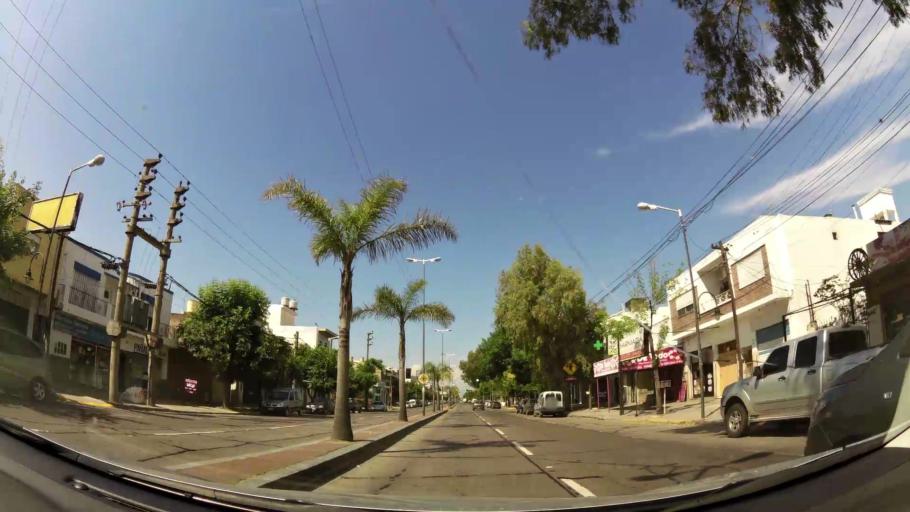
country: AR
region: Buenos Aires
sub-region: Partido de Tigre
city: Tigre
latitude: -34.4662
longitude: -58.5840
